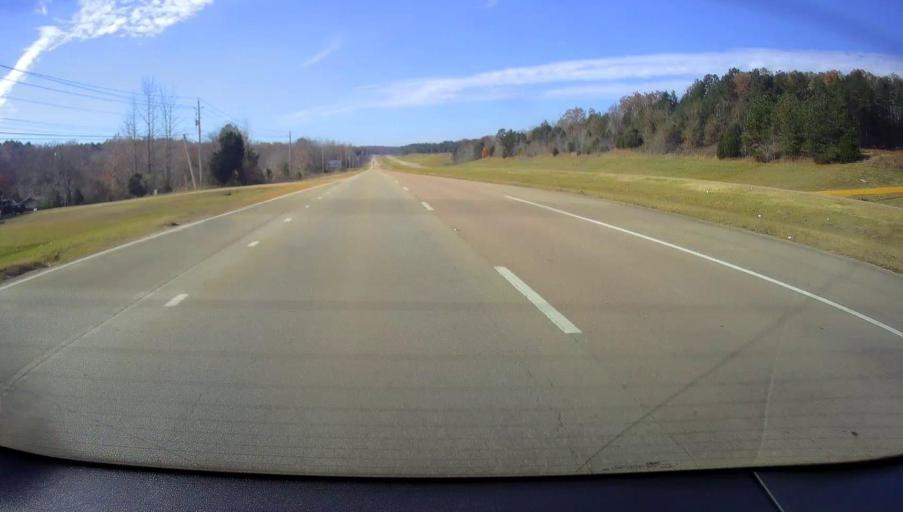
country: US
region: Mississippi
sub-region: Tippah County
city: Ripley
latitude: 34.9503
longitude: -88.9222
